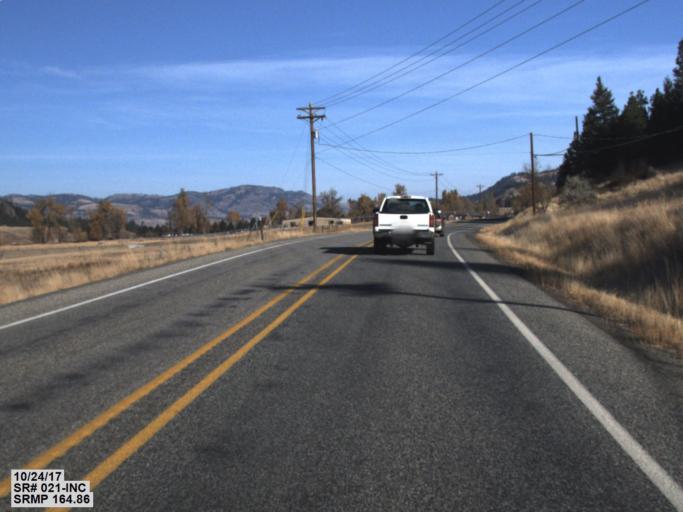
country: US
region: Washington
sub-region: Ferry County
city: Republic
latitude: 48.6719
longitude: -118.6669
